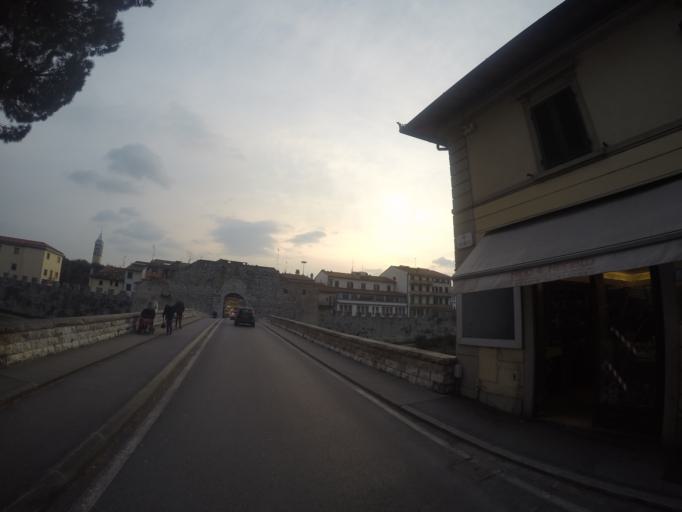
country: IT
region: Tuscany
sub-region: Provincia di Prato
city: Prato
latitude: 43.8813
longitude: 11.1032
